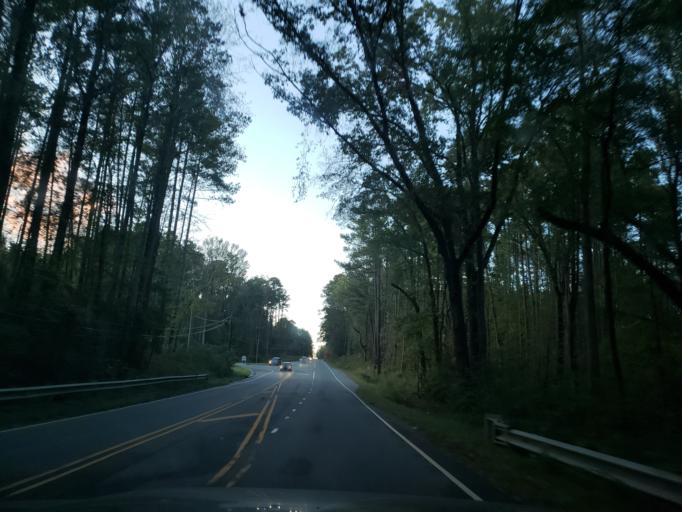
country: US
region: North Carolina
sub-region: Wake County
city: Green Level
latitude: 35.8704
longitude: -78.9461
